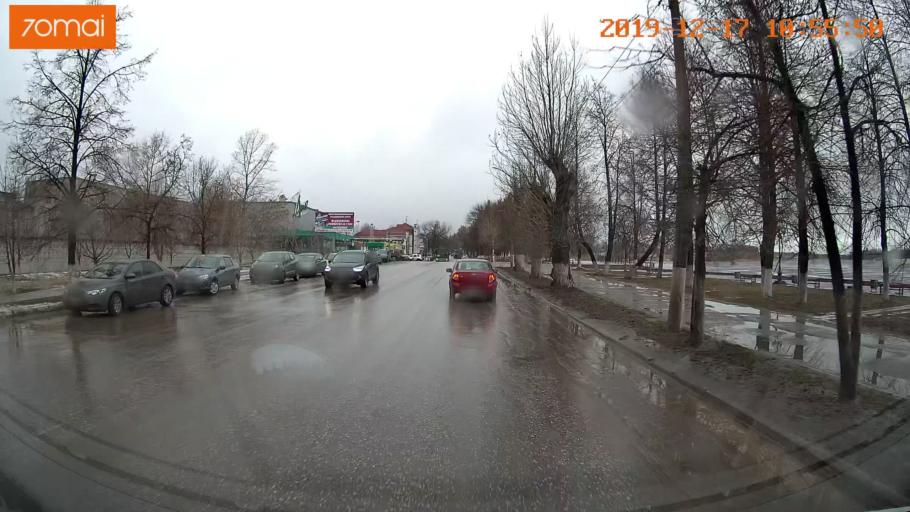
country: RU
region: Vladimir
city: Gus'-Khrustal'nyy
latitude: 55.6162
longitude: 40.6677
